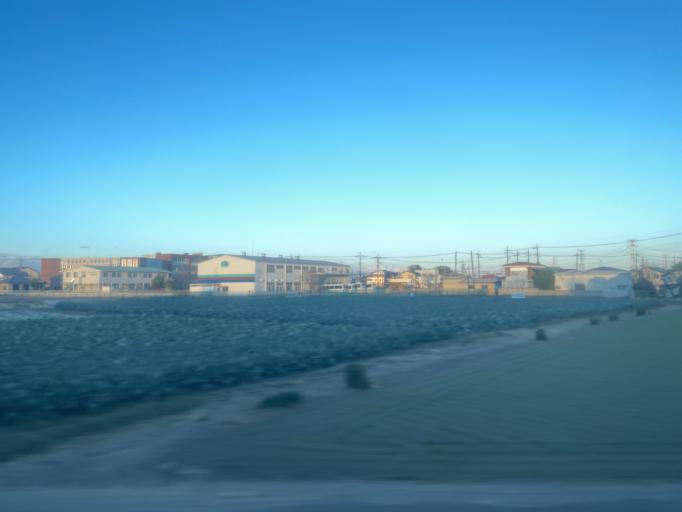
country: JP
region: Saitama
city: Honjo
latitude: 36.2242
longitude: 139.2051
